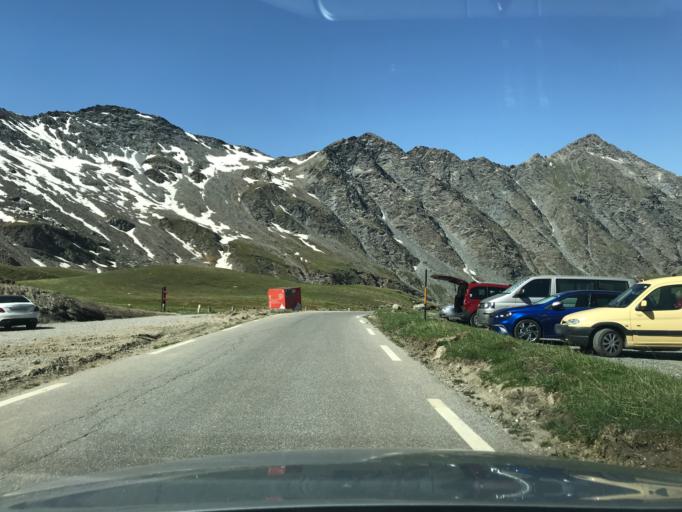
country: IT
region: Piedmont
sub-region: Provincia di Cuneo
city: Pontechianale
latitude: 44.6903
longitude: 6.9760
